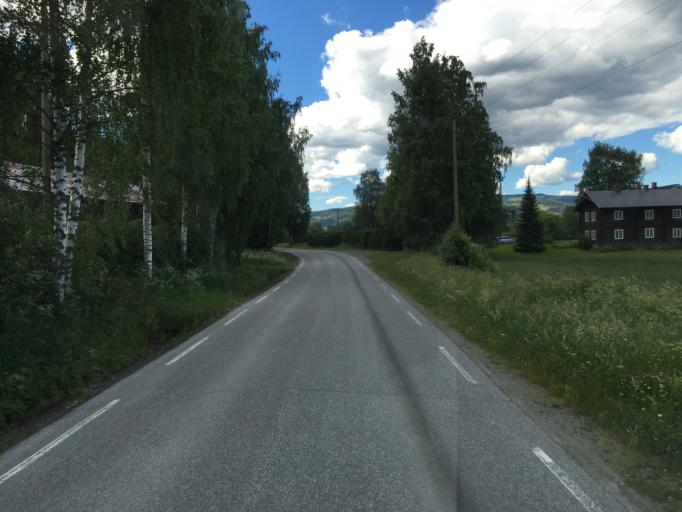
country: NO
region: Oppland
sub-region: Nordre Land
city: Dokka
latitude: 60.8135
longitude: 10.0954
